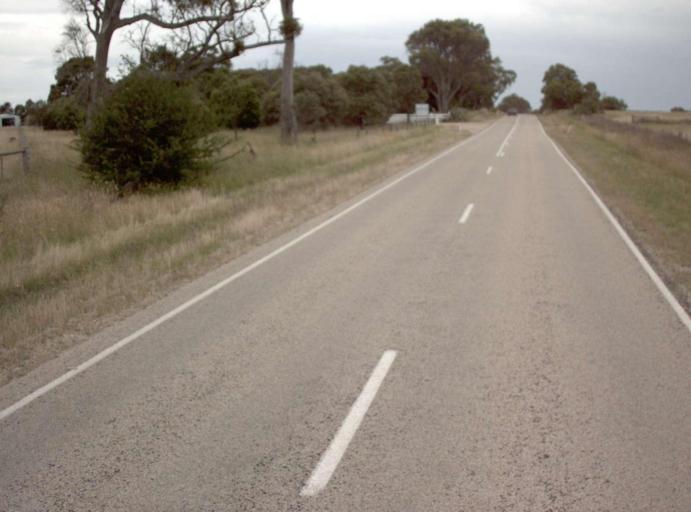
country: AU
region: Victoria
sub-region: East Gippsland
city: Bairnsdale
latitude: -37.9090
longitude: 147.5511
